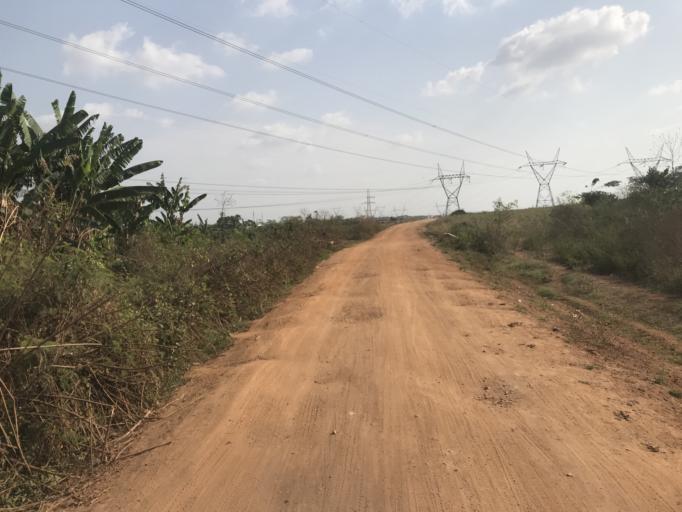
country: NG
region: Osun
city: Osogbo
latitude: 7.8339
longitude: 4.5712
